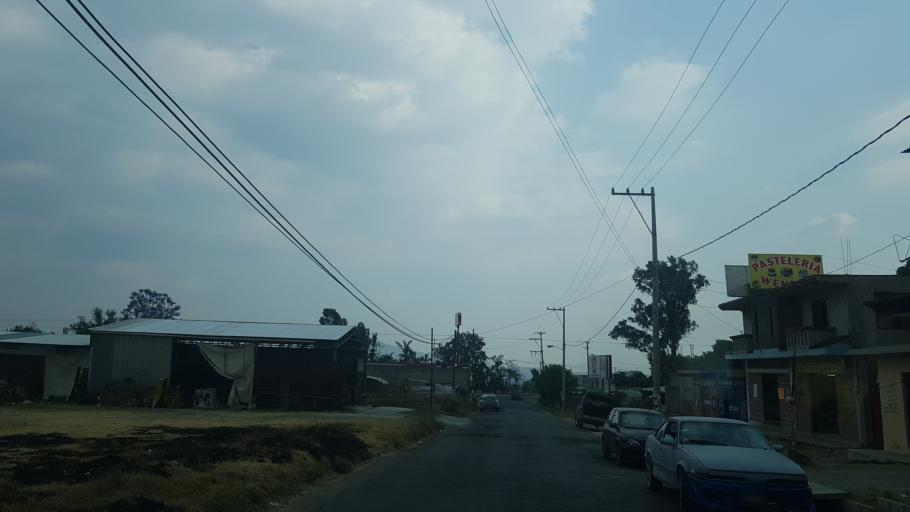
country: MX
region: Puebla
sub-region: Santa Isabel Cholula
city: Santa Ana Acozautla
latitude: 18.9449
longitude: -98.3947
